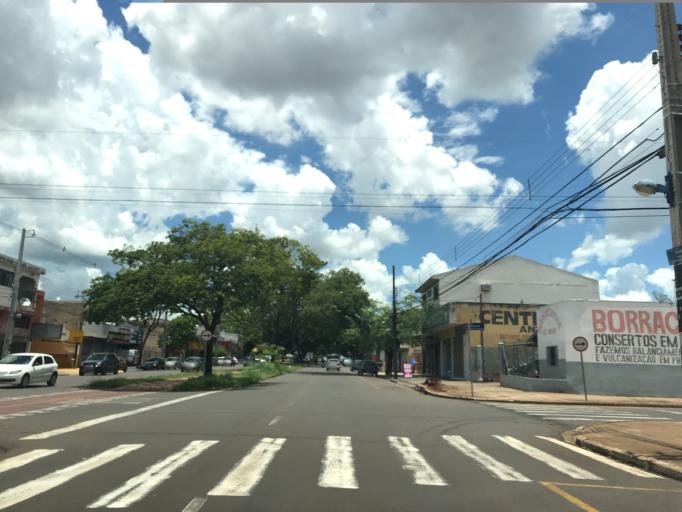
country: BR
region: Parana
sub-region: Maringa
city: Maringa
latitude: -23.3986
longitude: -51.9195
